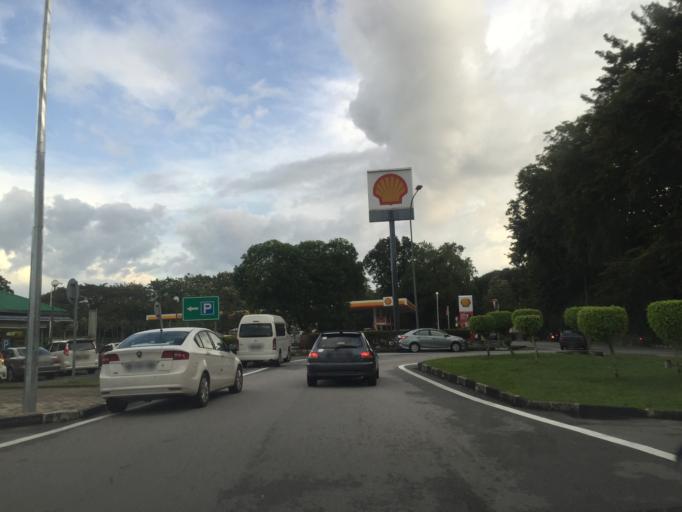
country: MY
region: Kedah
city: Gurun
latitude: 5.8307
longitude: 100.4890
